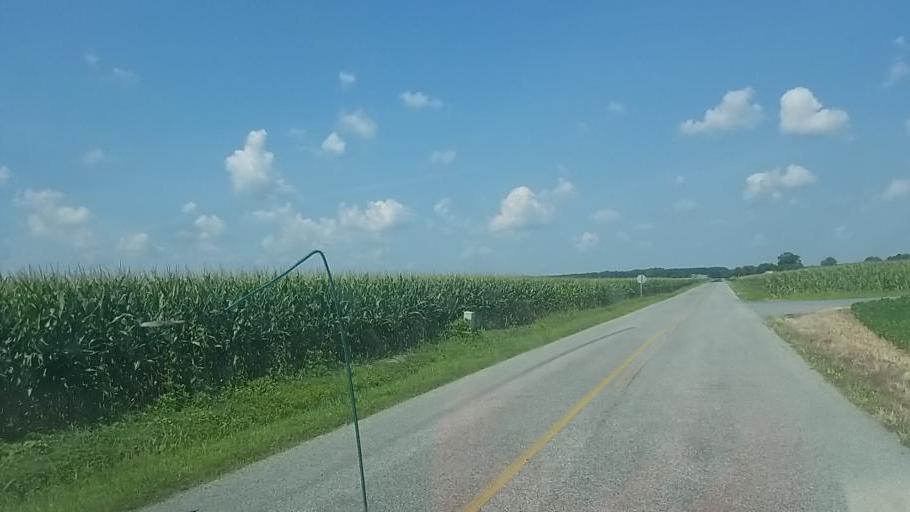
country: US
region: Maryland
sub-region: Worcester County
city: Berlin
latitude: 38.2944
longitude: -75.2531
